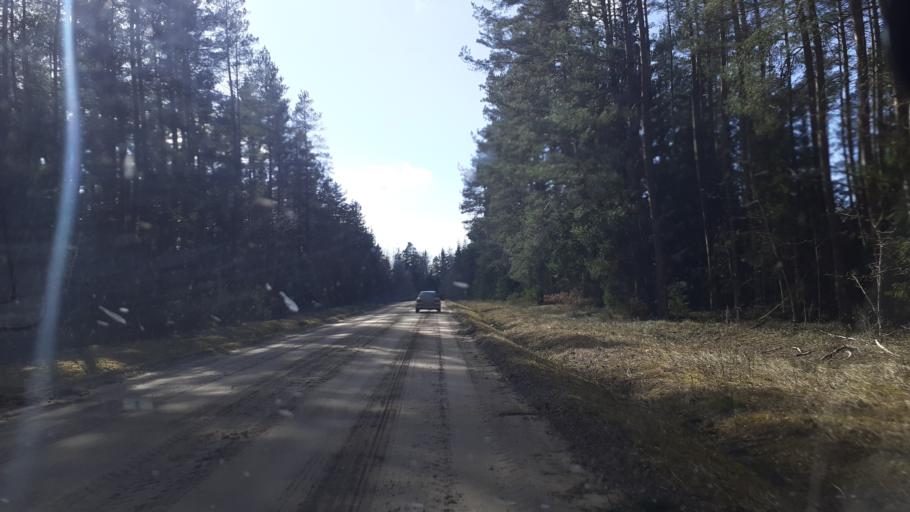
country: LV
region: Kuldigas Rajons
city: Kuldiga
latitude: 56.9094
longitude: 22.0750
